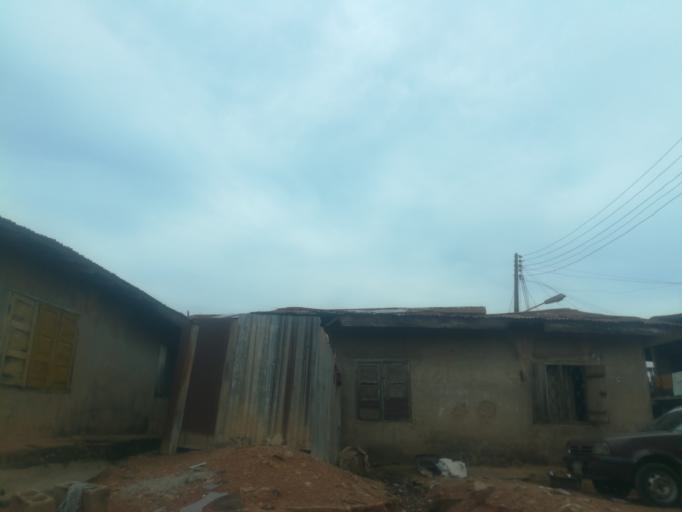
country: NG
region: Oyo
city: Ibadan
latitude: 7.3792
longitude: 3.9329
